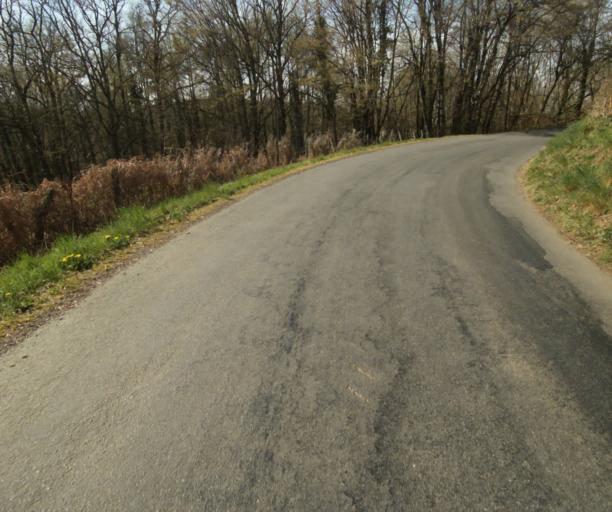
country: FR
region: Limousin
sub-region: Departement de la Correze
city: Naves
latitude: 45.3465
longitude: 1.7795
